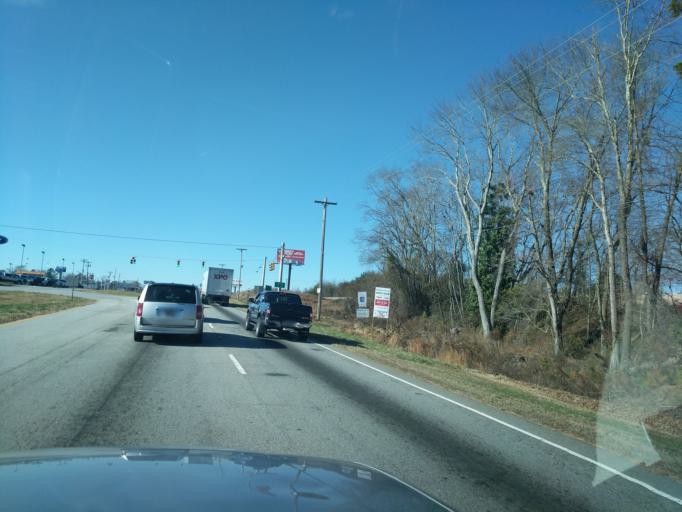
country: US
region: South Carolina
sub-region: Anderson County
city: Powdersville
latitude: 34.8277
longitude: -82.5367
